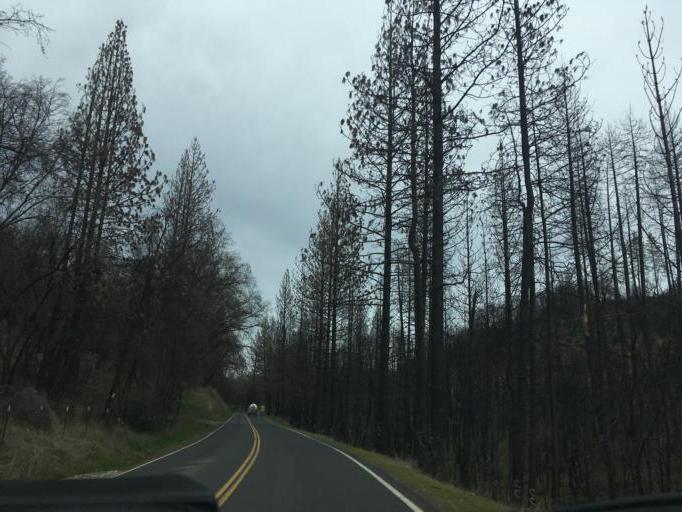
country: US
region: California
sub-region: Calaveras County
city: Mountain Ranch
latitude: 38.2350
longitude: -120.5254
